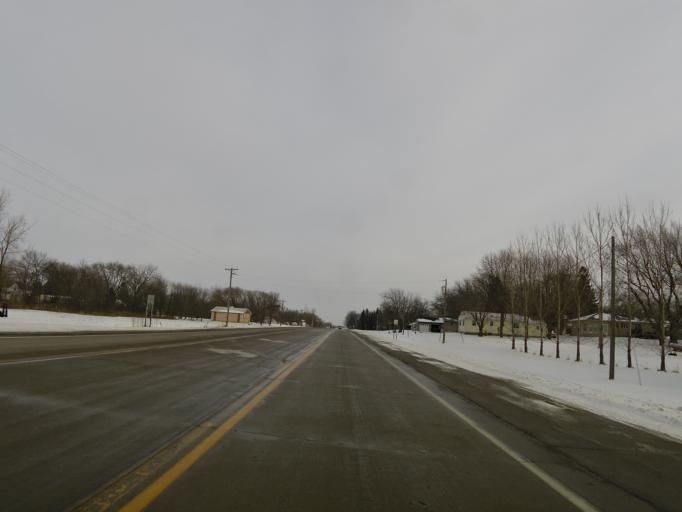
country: US
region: Minnesota
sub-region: McLeod County
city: Glencoe
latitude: 44.9062
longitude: -94.2024
